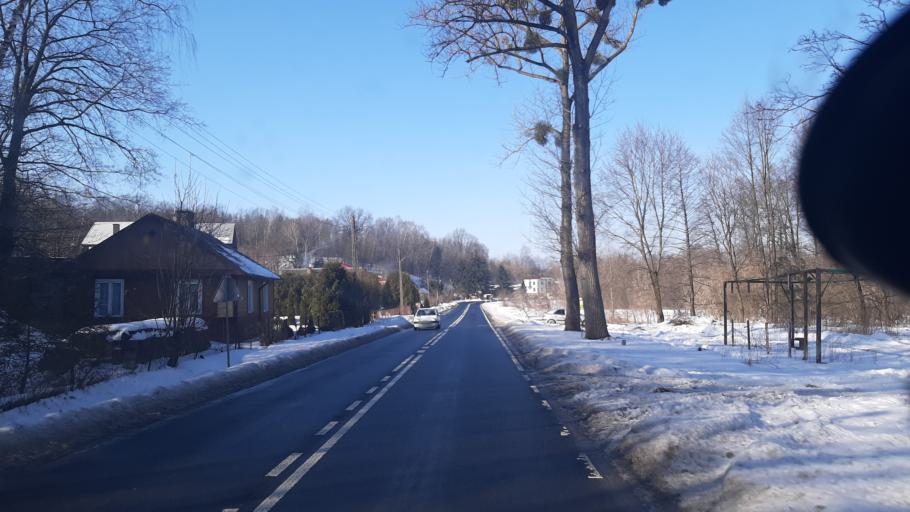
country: PL
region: Lublin Voivodeship
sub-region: Powiat pulawski
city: Wawolnica
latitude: 51.2903
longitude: 22.1589
